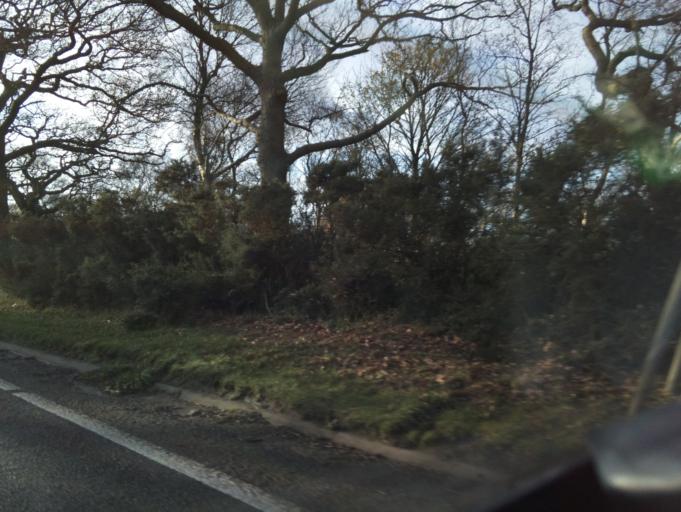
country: GB
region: England
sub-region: City and Borough of Birmingham
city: Sutton Coldfield
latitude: 52.5861
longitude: -1.7798
